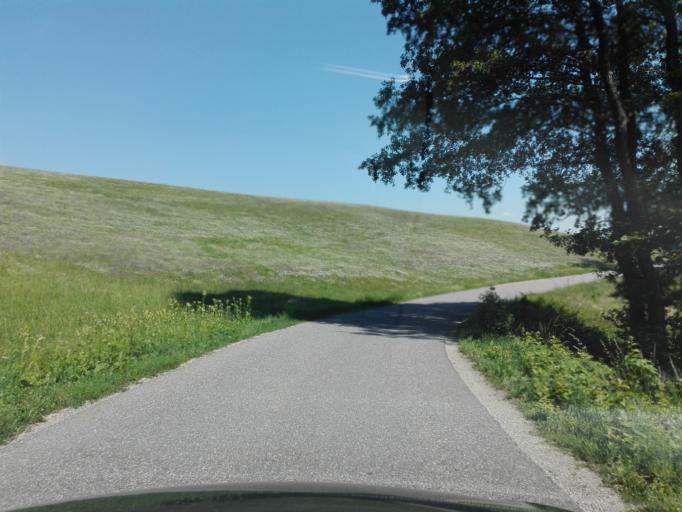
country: AT
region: Upper Austria
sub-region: Politischer Bezirk Urfahr-Umgebung
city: Steyregg
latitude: 48.3044
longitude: 14.3759
